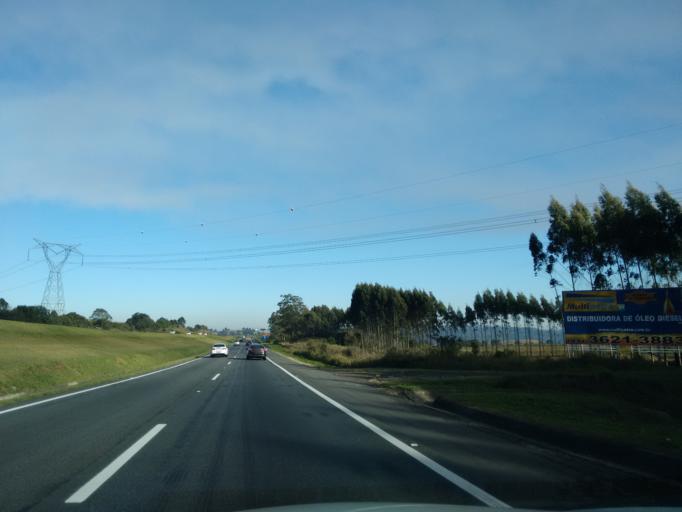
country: BR
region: Parana
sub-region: Campo Largo
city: Campo Largo
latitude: -25.4707
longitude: -49.6793
